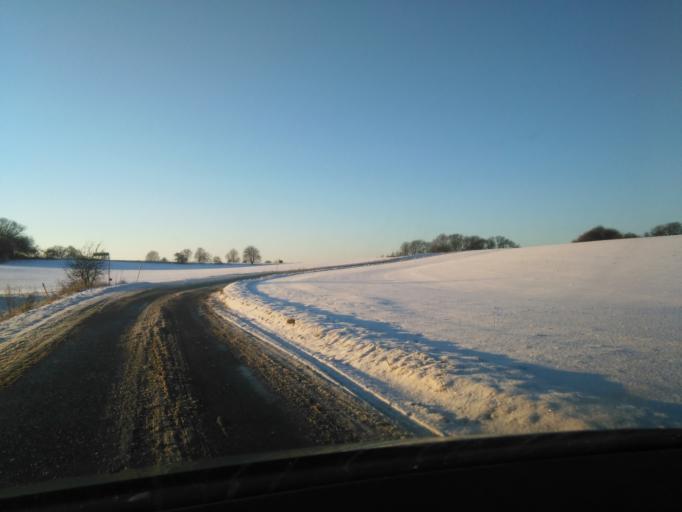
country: DK
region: Central Jutland
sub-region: Arhus Kommune
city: Tranbjerg
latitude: 56.0840
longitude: 10.1083
